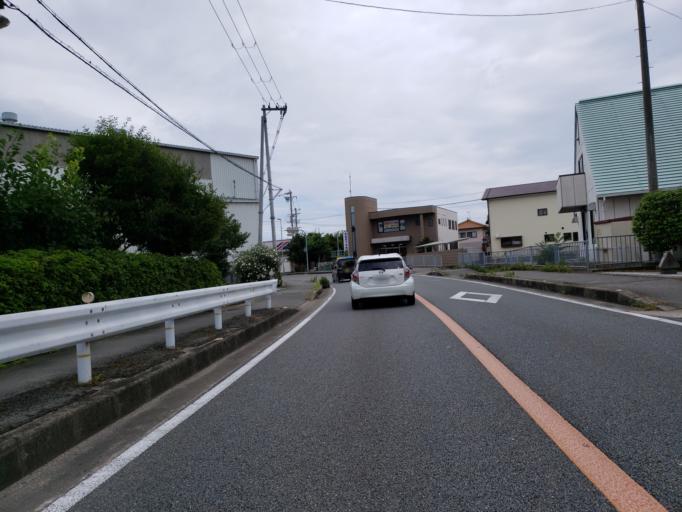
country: JP
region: Hyogo
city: Shirahamacho-usazakiminami
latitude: 34.7845
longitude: 134.7185
